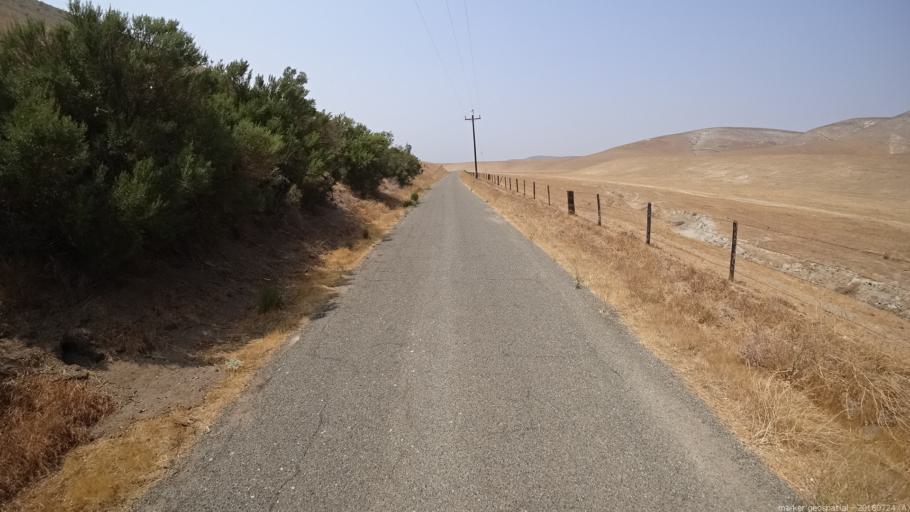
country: US
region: California
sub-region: Monterey County
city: King City
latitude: 36.1996
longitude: -121.0120
